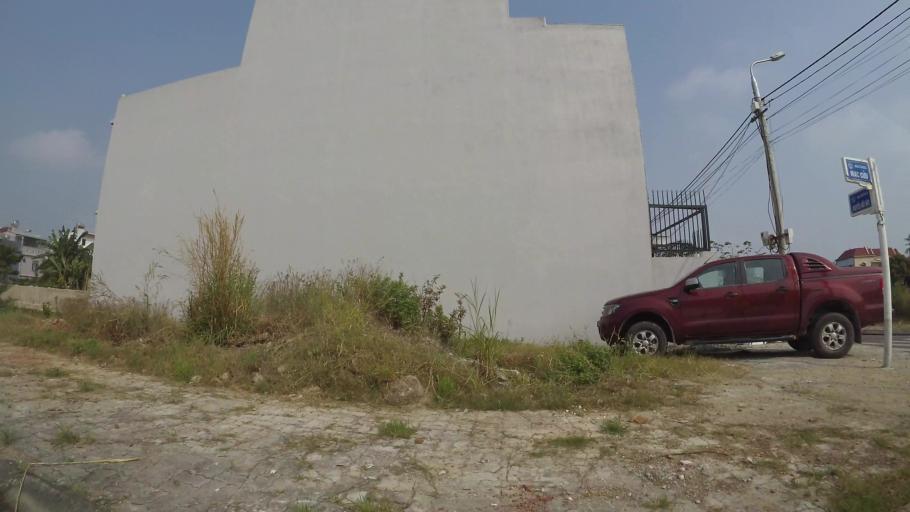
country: VN
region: Da Nang
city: Ngu Hanh Son
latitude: 16.0272
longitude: 108.2437
